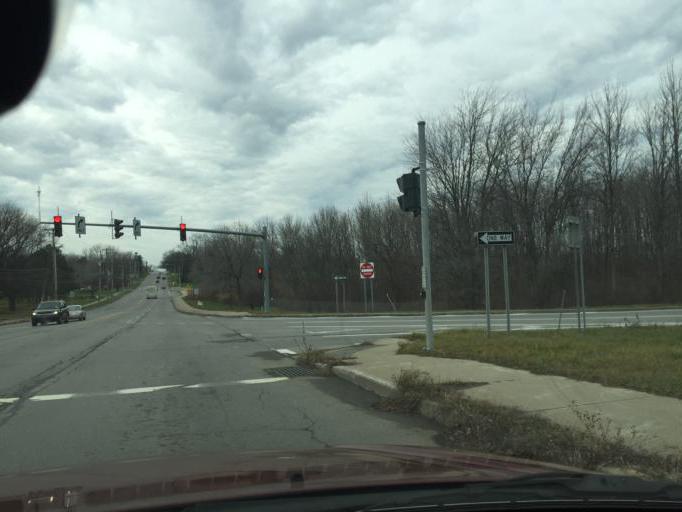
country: US
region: New York
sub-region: Monroe County
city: Rochester
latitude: 43.0952
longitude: -77.6031
